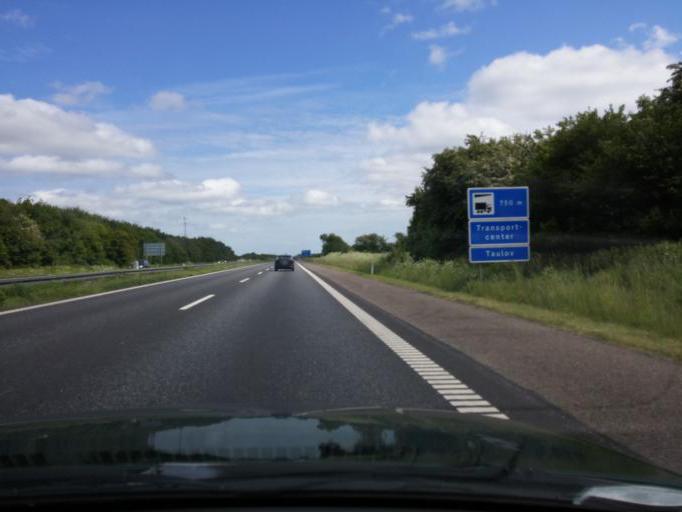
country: DK
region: South Denmark
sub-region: Fredericia Kommune
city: Taulov
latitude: 55.5408
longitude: 9.6193
